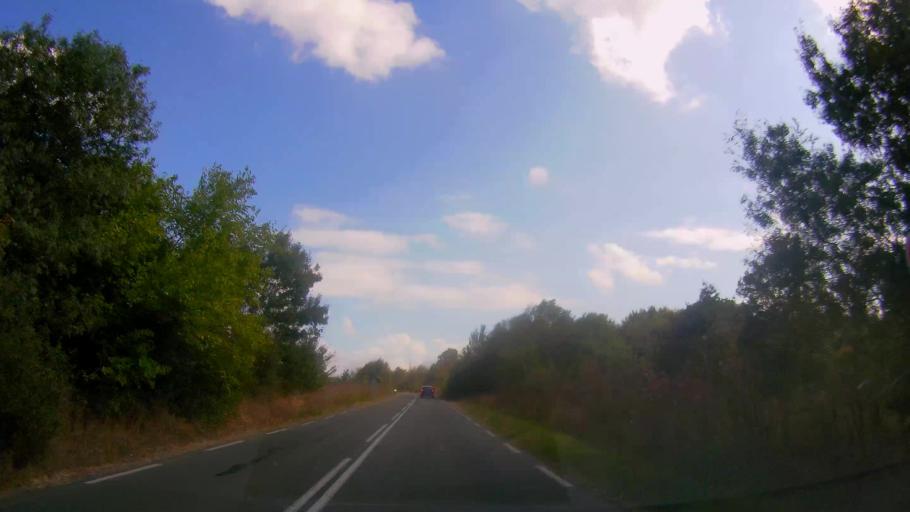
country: BG
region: Burgas
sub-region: Obshtina Kameno
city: Kameno
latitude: 42.4807
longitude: 27.3462
